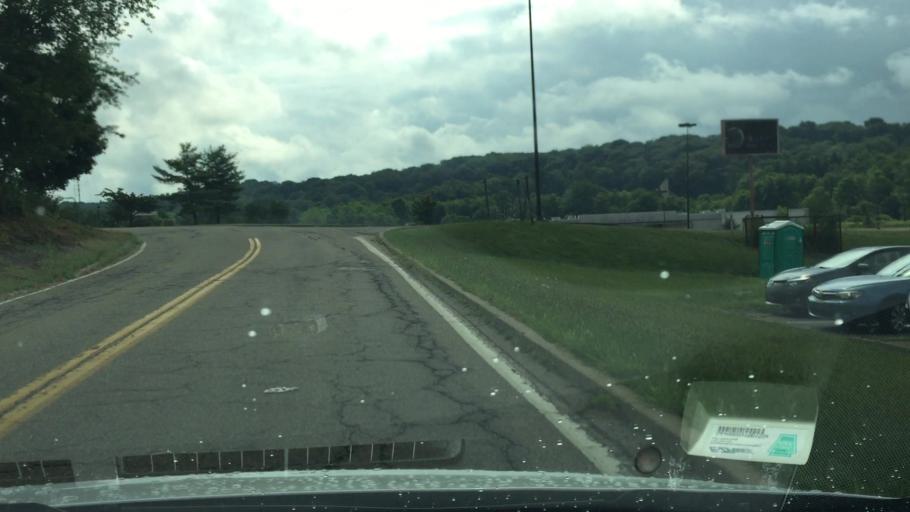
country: US
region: Pennsylvania
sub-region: Allegheny County
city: Franklin Park
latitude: 40.5868
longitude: -80.0295
